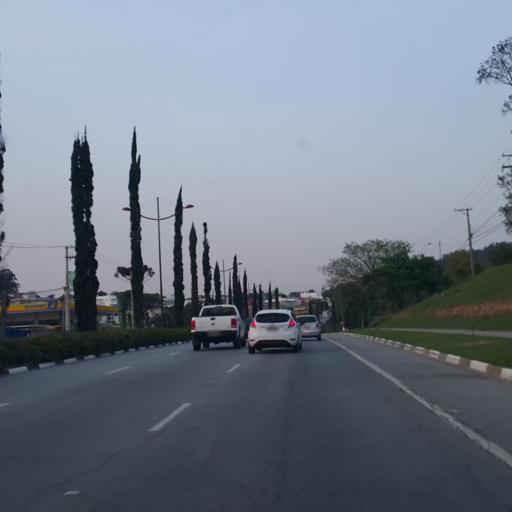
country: BR
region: Sao Paulo
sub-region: Vinhedo
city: Vinhedo
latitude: -23.0563
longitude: -46.9903
